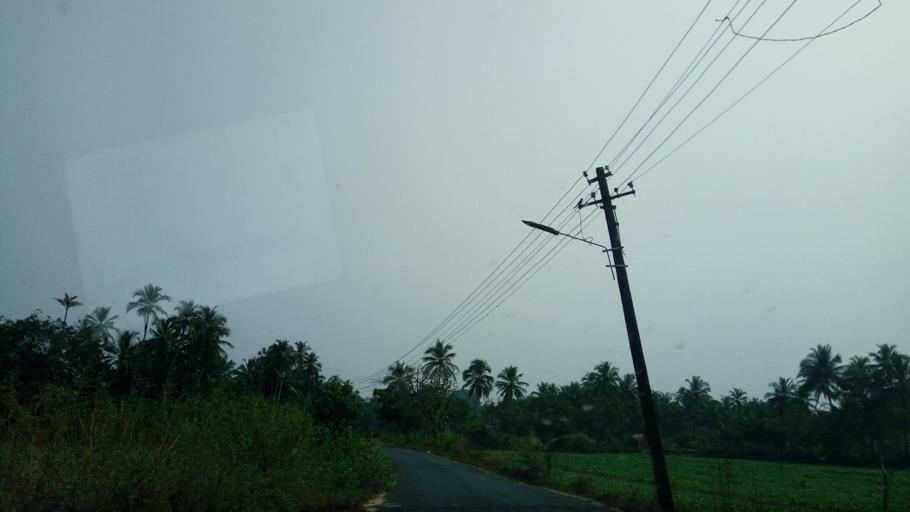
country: IN
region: Goa
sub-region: South Goa
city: Varca
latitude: 15.2211
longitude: 73.9403
